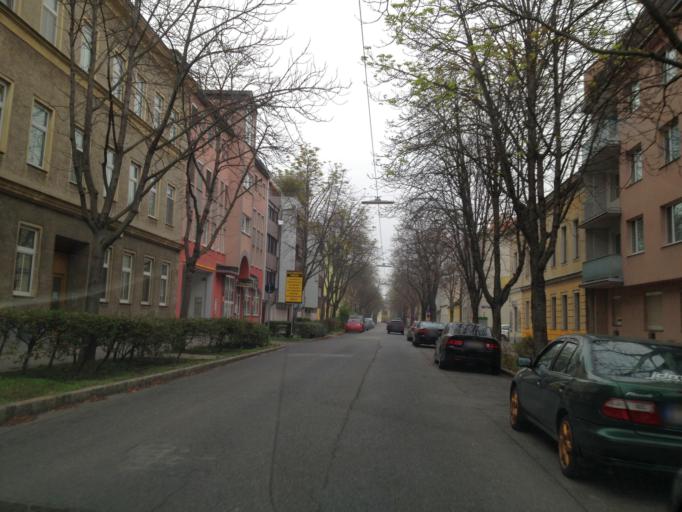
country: AT
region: Lower Austria
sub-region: Politischer Bezirk Korneuburg
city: Langenzersdorf
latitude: 48.2668
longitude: 16.3856
